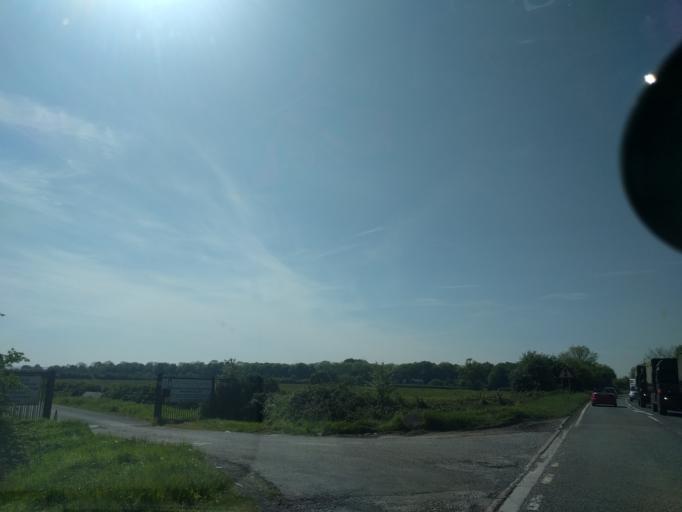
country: GB
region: England
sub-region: Somerset
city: Ilchester
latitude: 51.0269
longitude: -2.6626
